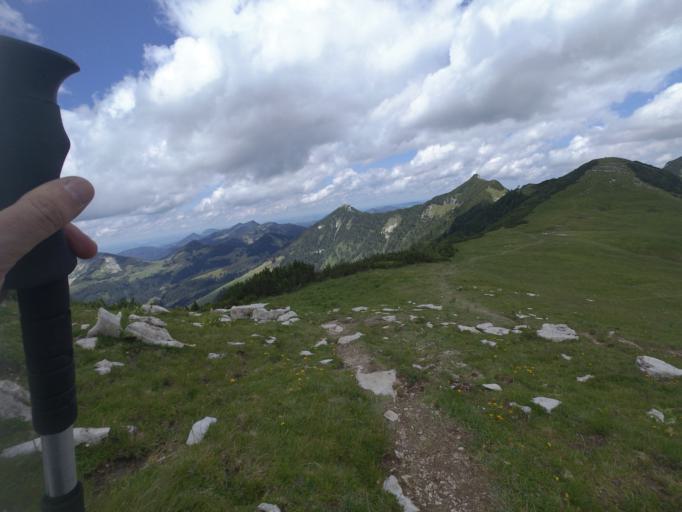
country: AT
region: Salzburg
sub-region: Politischer Bezirk Salzburg-Umgebung
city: Hintersee
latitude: 47.6627
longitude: 13.2967
